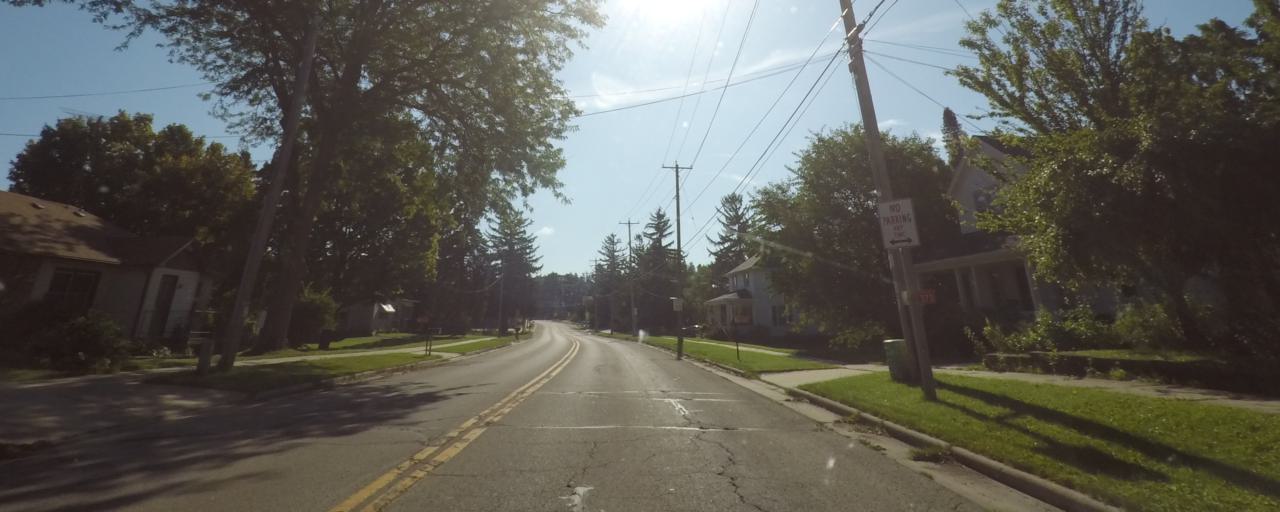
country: US
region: Wisconsin
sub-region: Jefferson County
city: Johnson Creek
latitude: 43.0127
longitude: -88.7030
